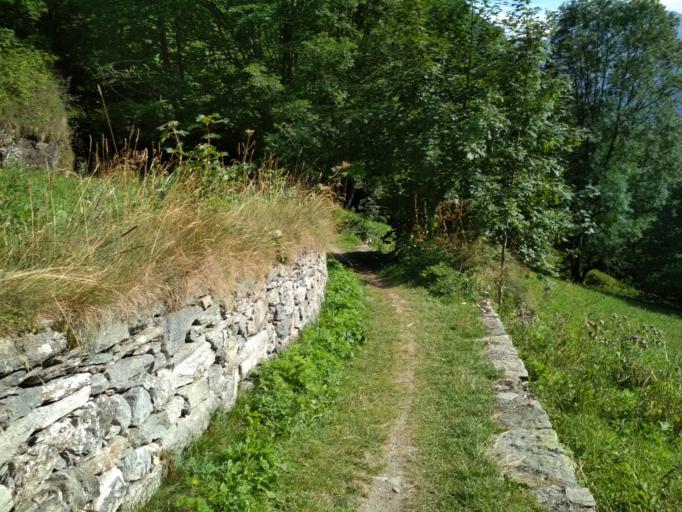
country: IT
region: Aosta Valley
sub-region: Valle d'Aosta
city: Gressoney-La-Trinite
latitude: 45.8083
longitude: 7.8266
